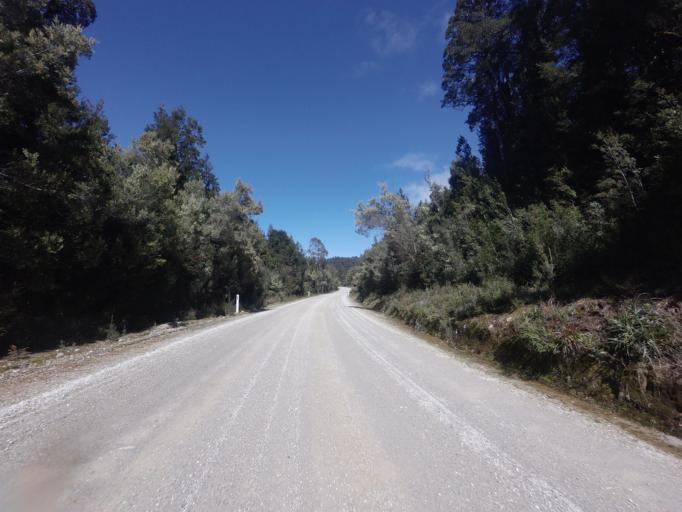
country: AU
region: Tasmania
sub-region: Huon Valley
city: Geeveston
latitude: -42.8342
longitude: 146.3820
